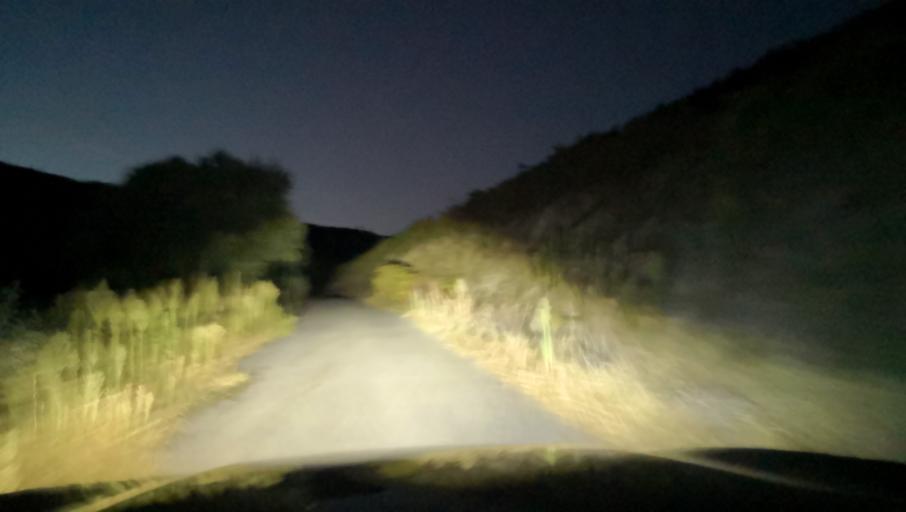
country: PT
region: Viseu
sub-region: Armamar
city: Armamar
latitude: 41.1532
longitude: -7.6961
